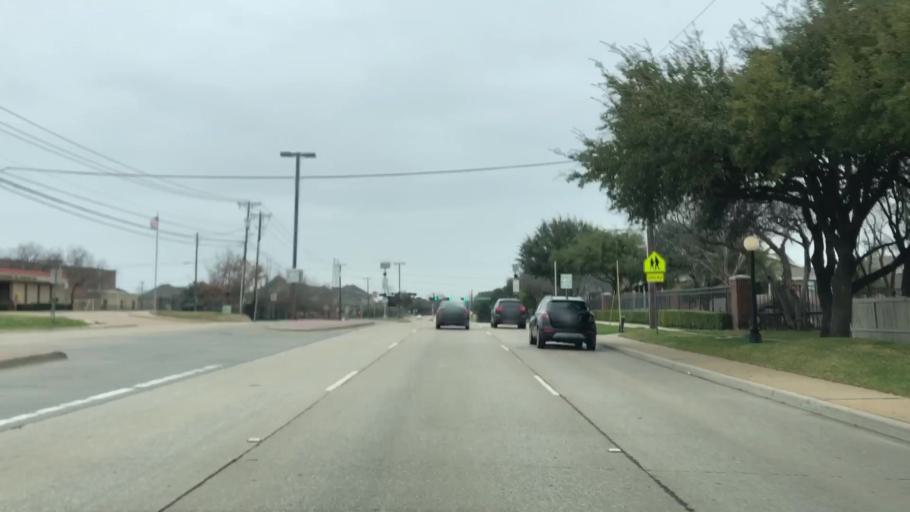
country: US
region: Texas
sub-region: Dallas County
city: Addison
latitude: 32.9726
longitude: -96.8556
